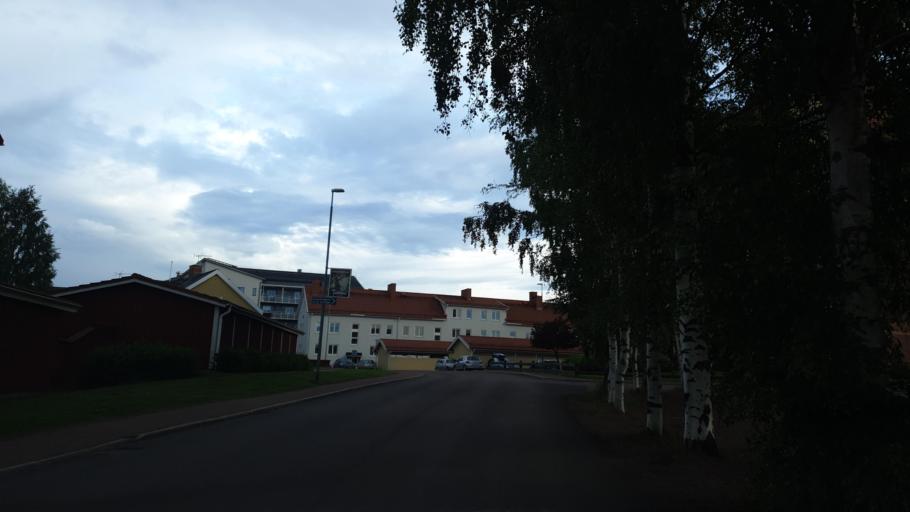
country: SE
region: Dalarna
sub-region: Mora Kommun
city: Mora
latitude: 61.0067
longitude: 14.5328
